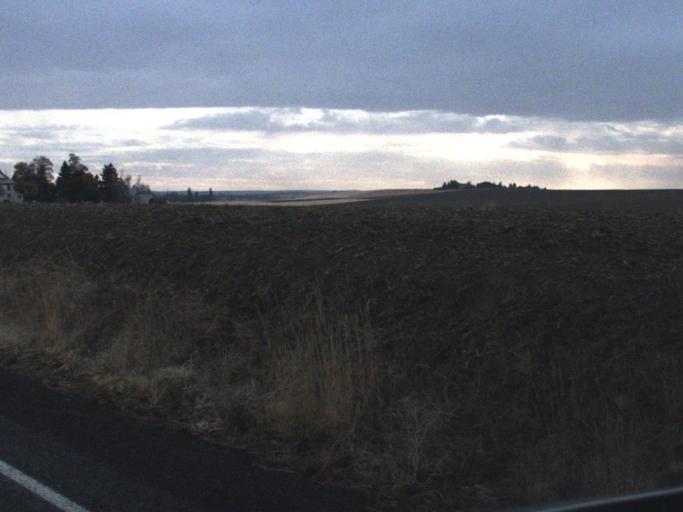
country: US
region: Washington
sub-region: Lincoln County
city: Davenport
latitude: 47.7944
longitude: -118.1737
